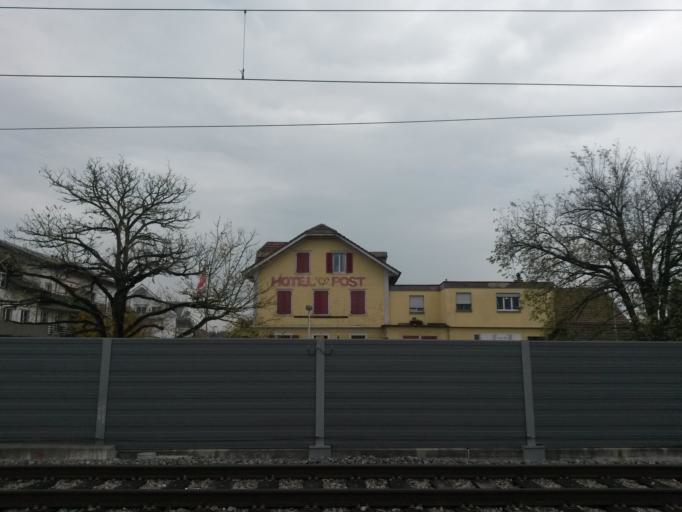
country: CH
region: Solothurn
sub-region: Bezirk Wasseramt
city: Luterbach
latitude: 47.2179
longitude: 7.5853
